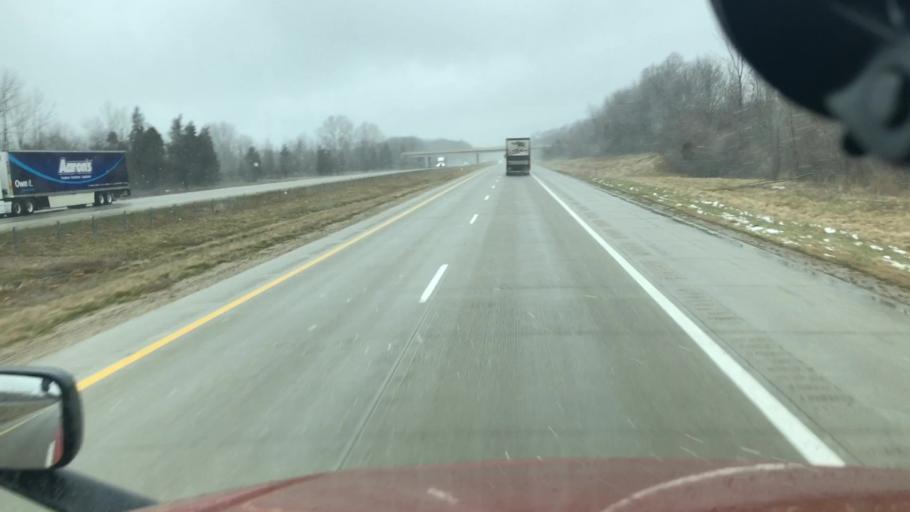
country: US
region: Michigan
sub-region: Allegan County
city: Douglas
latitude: 42.5458
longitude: -86.2187
